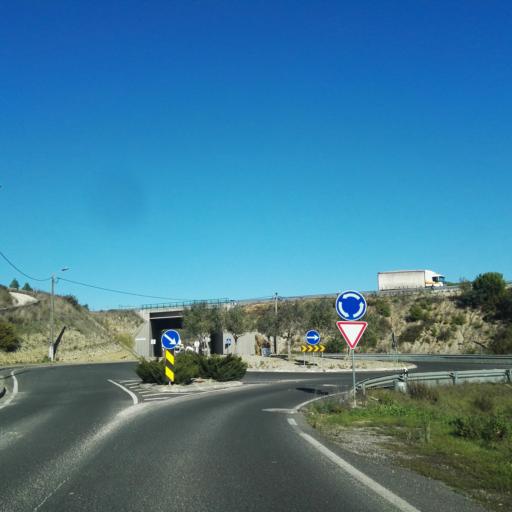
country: PT
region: Lisbon
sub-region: Mafra
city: Venda do Pinheiro
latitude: 38.9378
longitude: -9.2320
